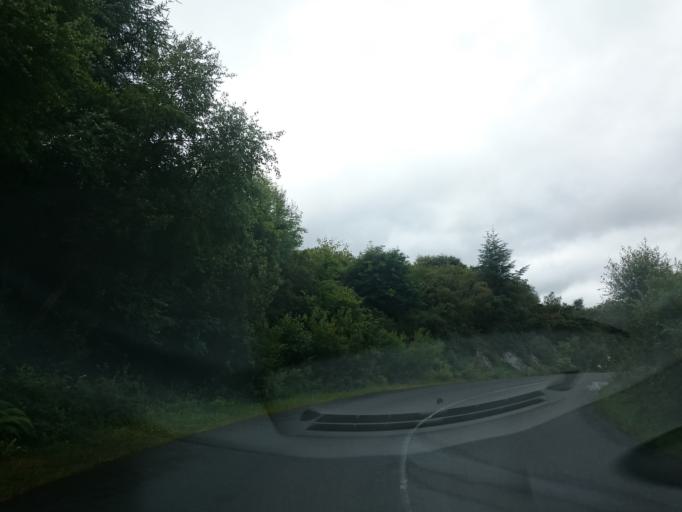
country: IE
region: Connaught
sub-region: County Galway
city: Clifden
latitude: 53.5513
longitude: -9.9506
